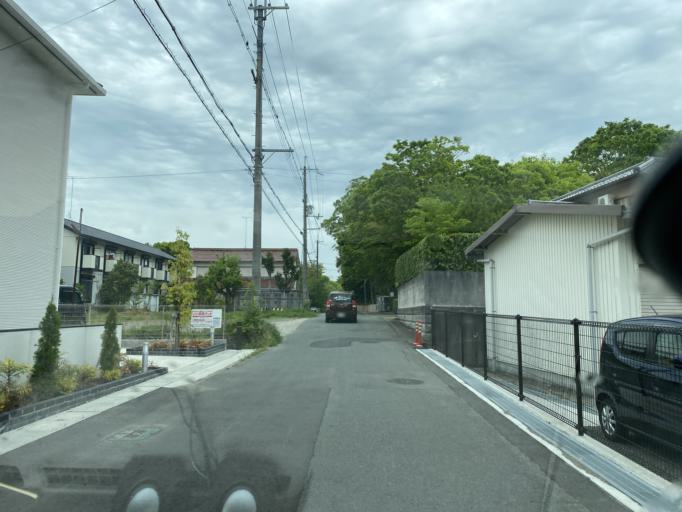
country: JP
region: Hyogo
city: Sasayama
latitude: 35.0699
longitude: 135.2171
